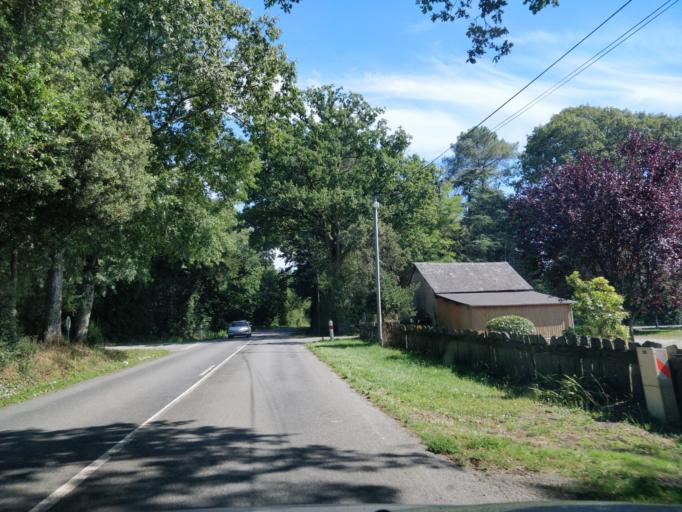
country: FR
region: Pays de la Loire
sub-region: Departement de la Loire-Atlantique
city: Guemene-Penfao
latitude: 47.6508
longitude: -1.7932
